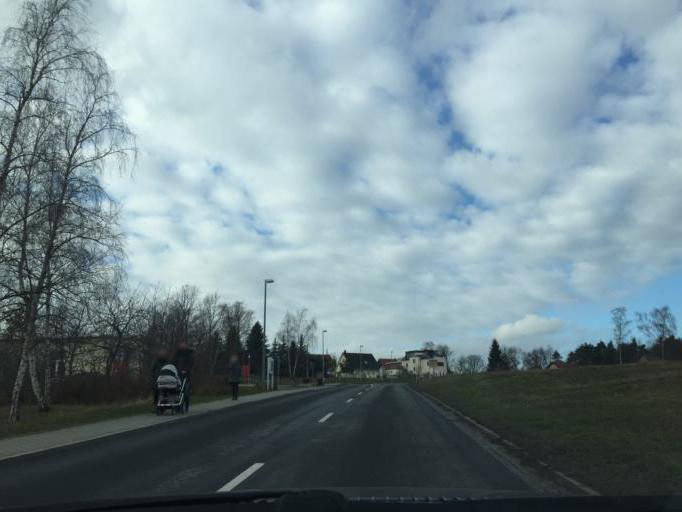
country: DE
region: Saxony
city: Ottendorf-Okrilla
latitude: 51.1837
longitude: 13.7863
